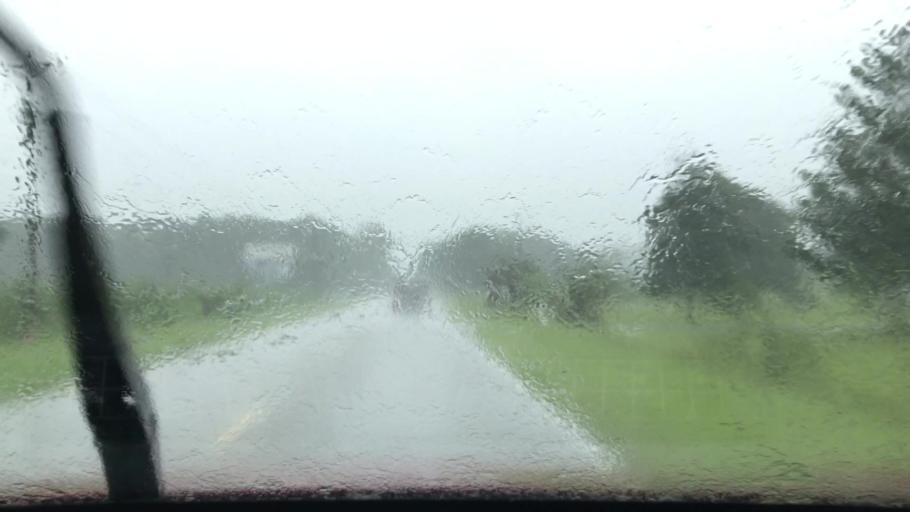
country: US
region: South Carolina
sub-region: Horry County
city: Red Hill
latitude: 33.8959
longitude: -78.9367
